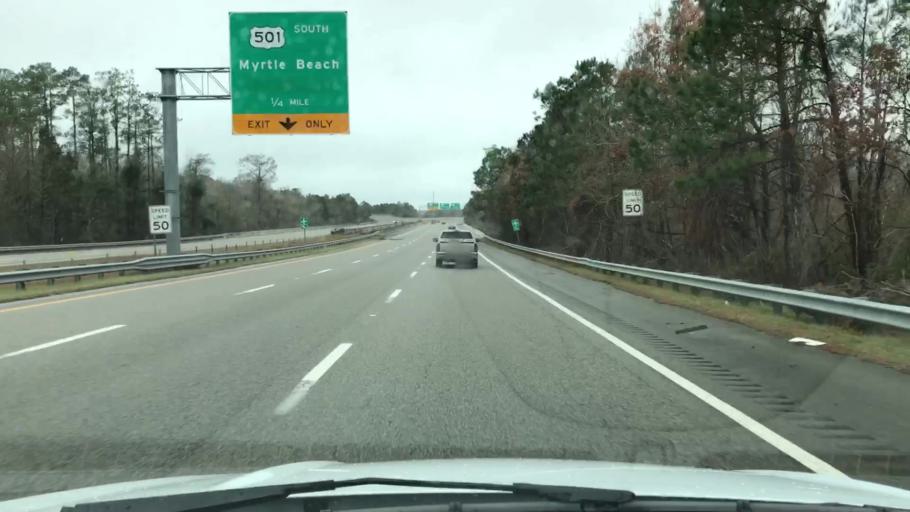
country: US
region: South Carolina
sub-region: Horry County
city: Forestbrook
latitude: 33.7419
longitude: -78.9416
